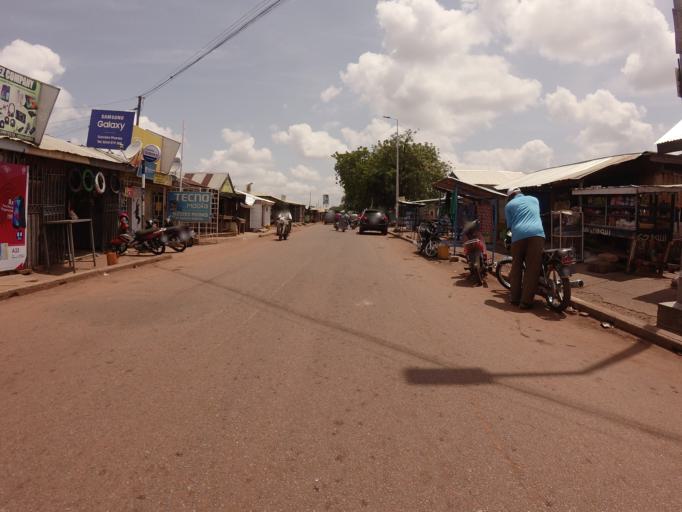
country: GH
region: Northern
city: Tamale
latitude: 9.4015
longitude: -0.8427
